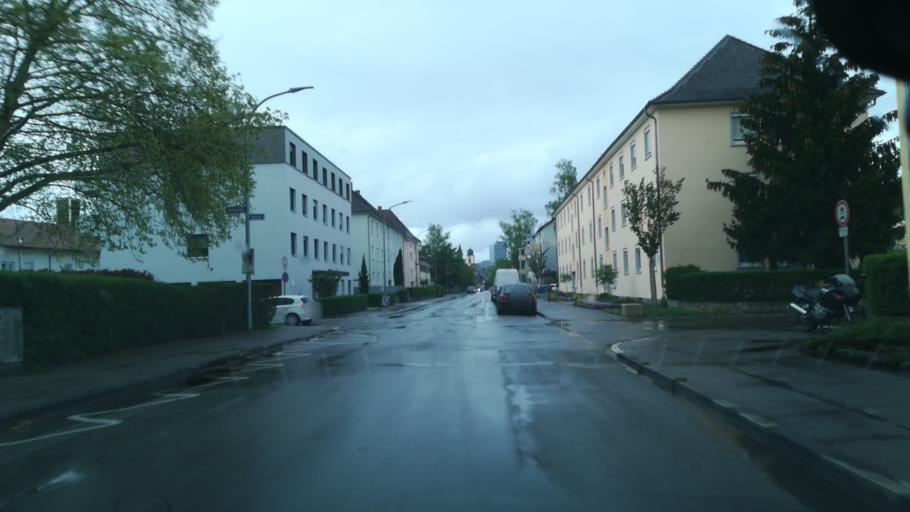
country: DE
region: Baden-Wuerttemberg
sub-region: Freiburg Region
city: Singen
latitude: 47.7480
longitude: 8.8456
